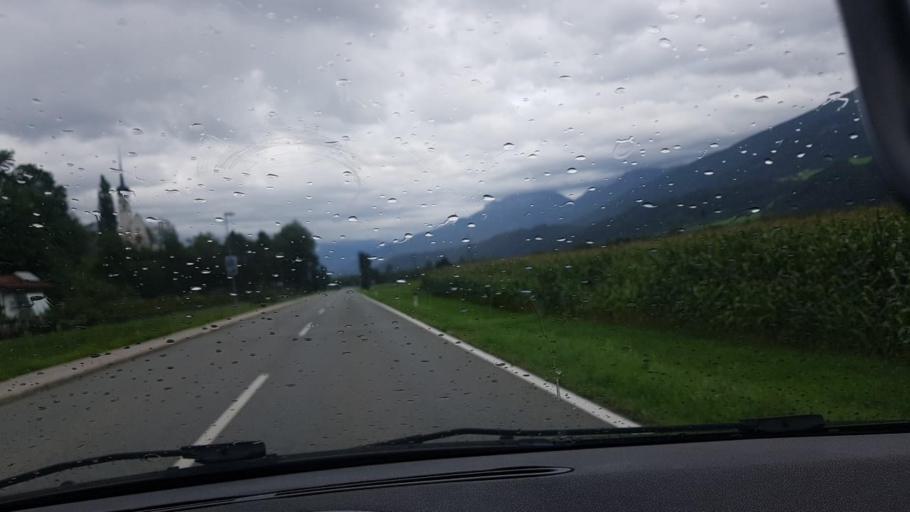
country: AT
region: Tyrol
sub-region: Politischer Bezirk Innsbruck Land
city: Hatting
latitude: 47.2902
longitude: 11.1653
